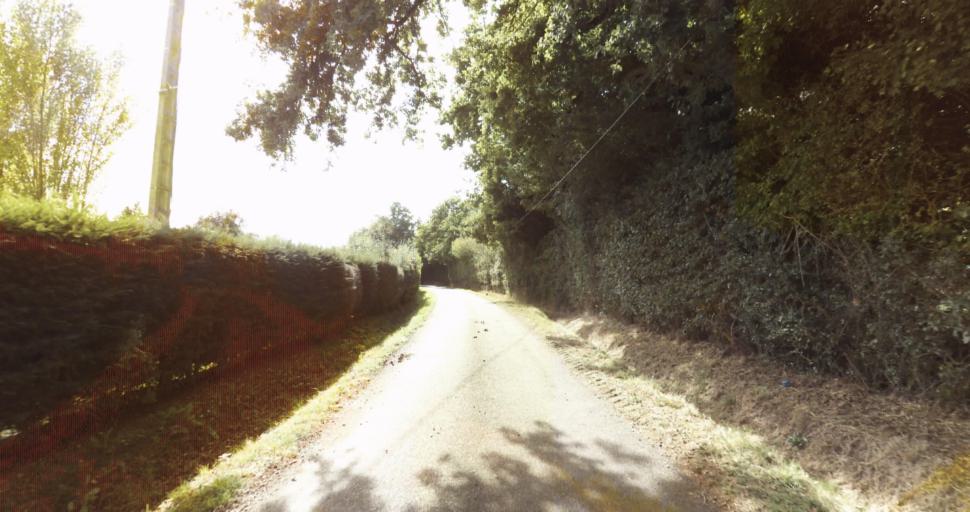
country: FR
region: Lower Normandy
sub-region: Departement de l'Orne
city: Sees
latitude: 48.6971
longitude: 0.1883
